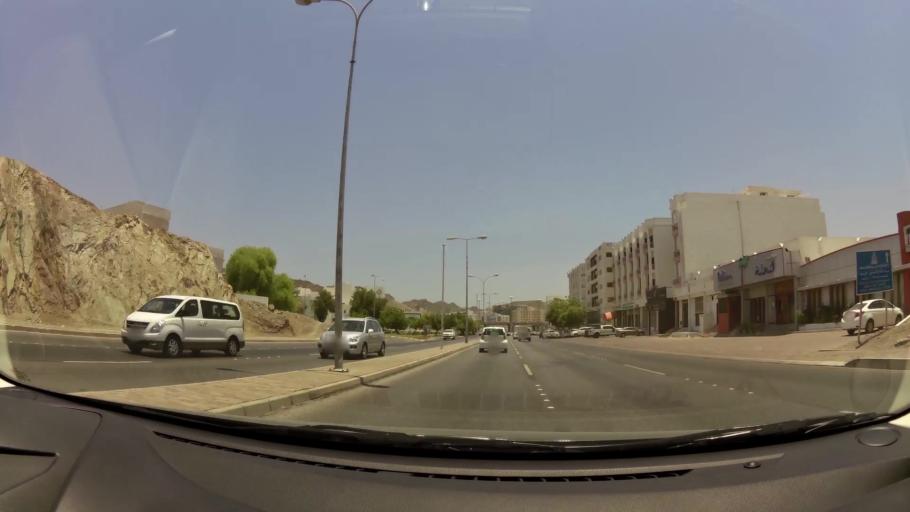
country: OM
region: Muhafazat Masqat
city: Muscat
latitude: 23.6126
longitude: 58.5423
